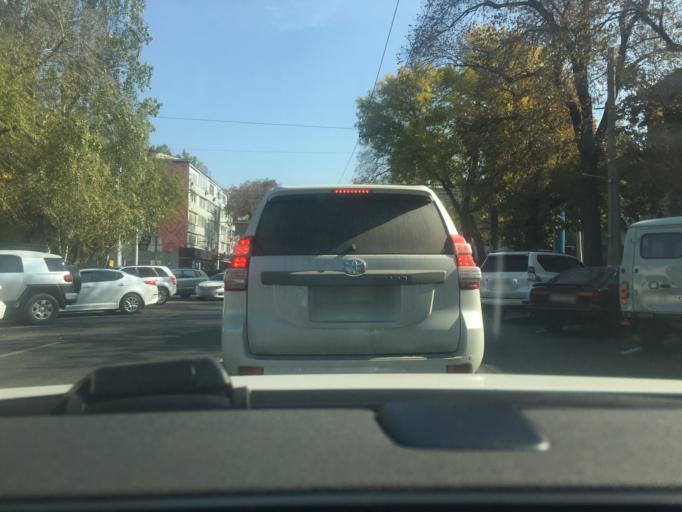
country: KZ
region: Almaty Qalasy
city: Almaty
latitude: 43.2615
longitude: 76.9382
